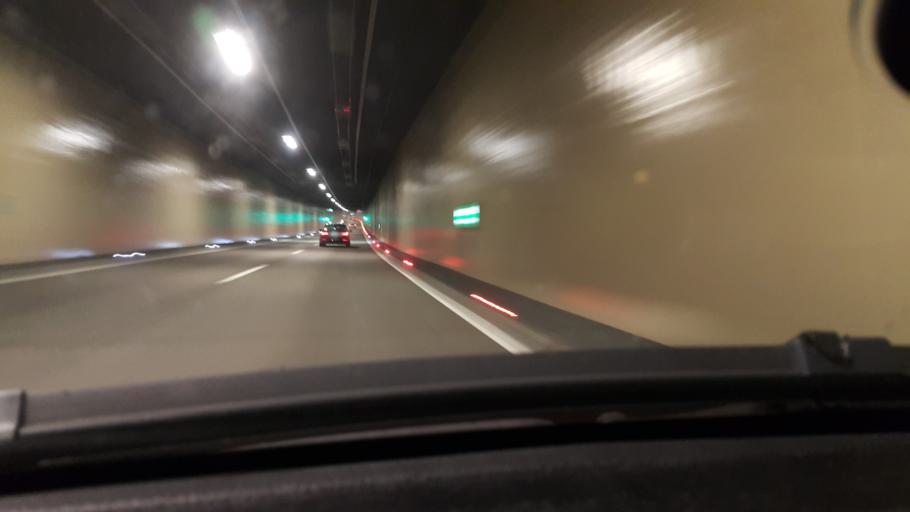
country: AT
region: Carinthia
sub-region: Klagenfurt am Woerthersee
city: Klagenfurt am Woerthersee
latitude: 46.6488
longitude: 14.3278
